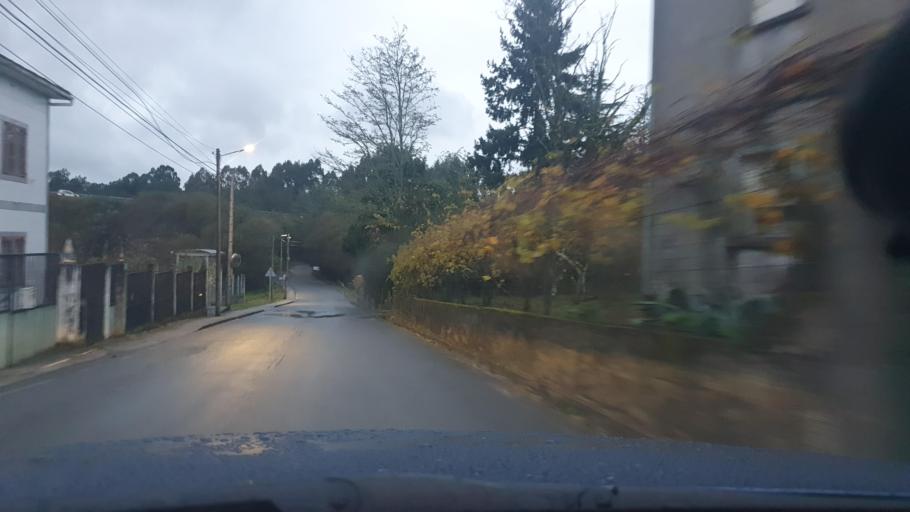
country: ES
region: Galicia
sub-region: Provincia da Coruna
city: Santiago de Compostela
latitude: 42.8476
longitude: -8.5919
